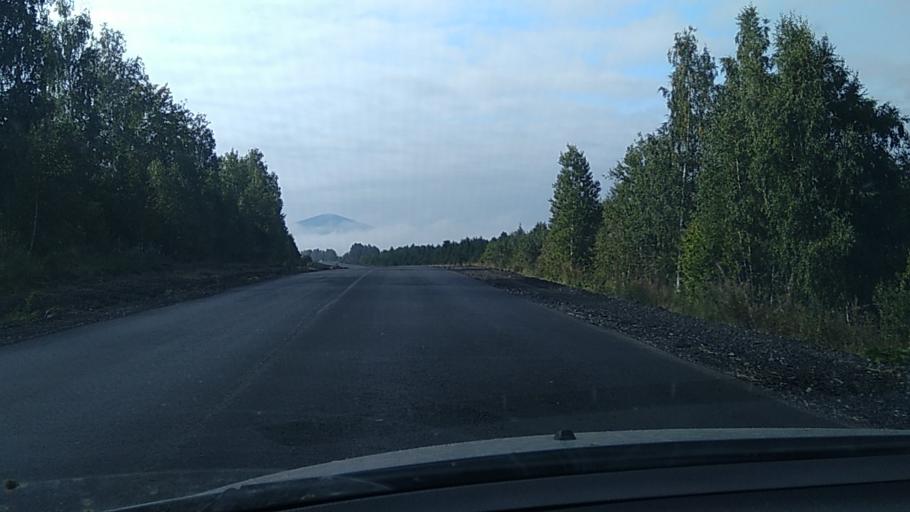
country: RU
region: Chelyabinsk
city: Karabash
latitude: 55.3660
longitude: 60.2456
